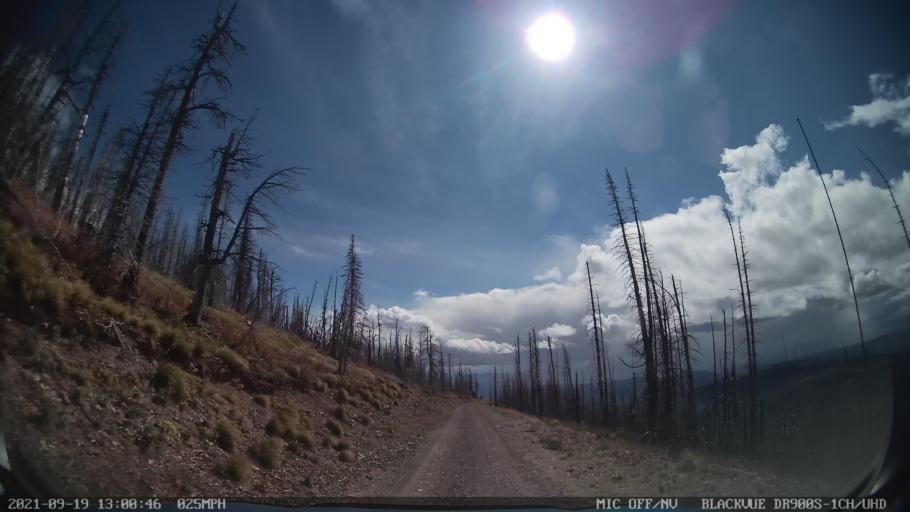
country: US
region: Montana
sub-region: Missoula County
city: Seeley Lake
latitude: 47.1868
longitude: -113.3579
